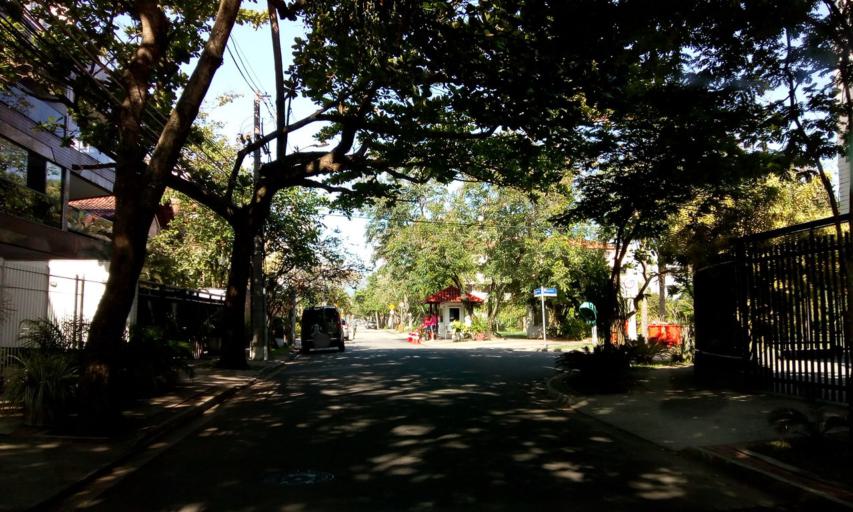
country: BR
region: Rio de Janeiro
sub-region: Nilopolis
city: Nilopolis
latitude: -23.0169
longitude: -43.4551
